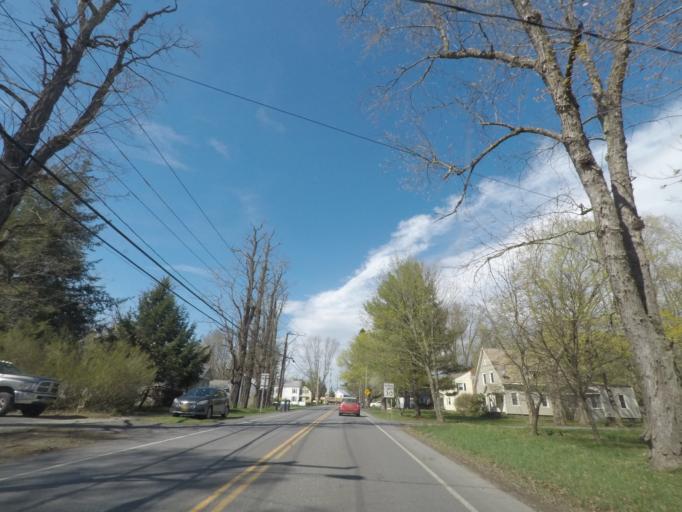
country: US
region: New York
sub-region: Greene County
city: Cairo
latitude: 42.4186
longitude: -74.0218
